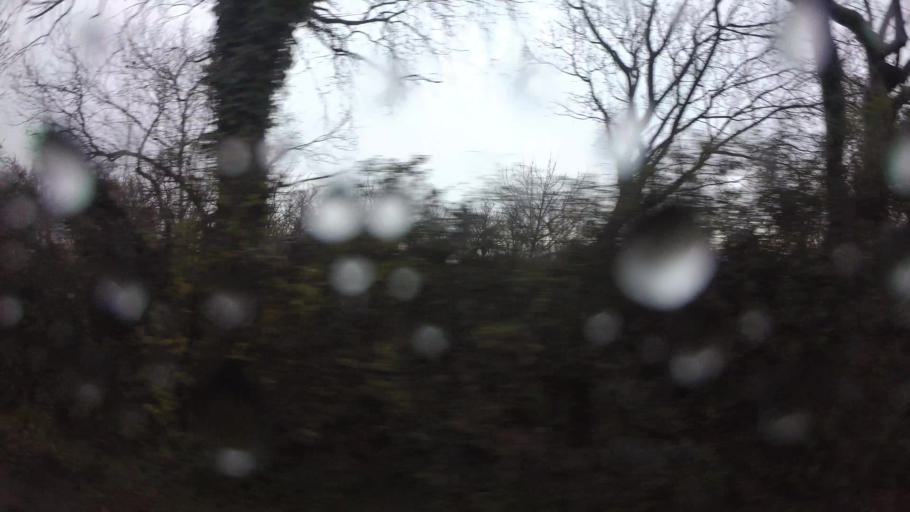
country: BA
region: Federation of Bosnia and Herzegovina
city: Cim
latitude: 43.3507
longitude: 17.7803
